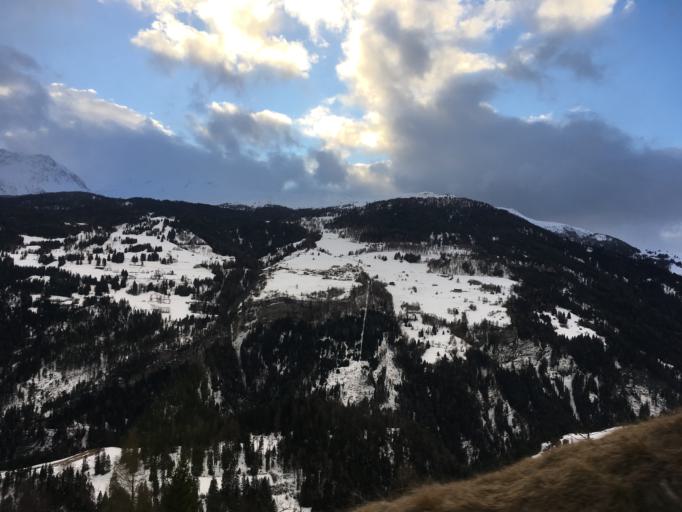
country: CH
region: Grisons
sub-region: Albula District
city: Tiefencastel
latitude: 46.6764
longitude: 9.5674
